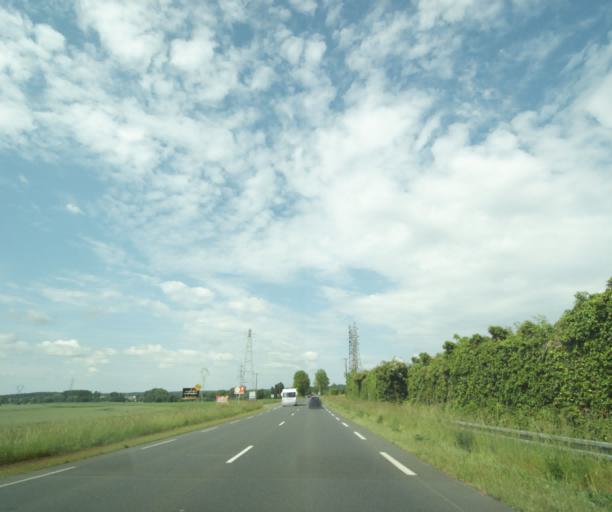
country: FR
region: Pays de la Loire
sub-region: Departement de Maine-et-Loire
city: Distre
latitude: 47.2095
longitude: -0.1182
